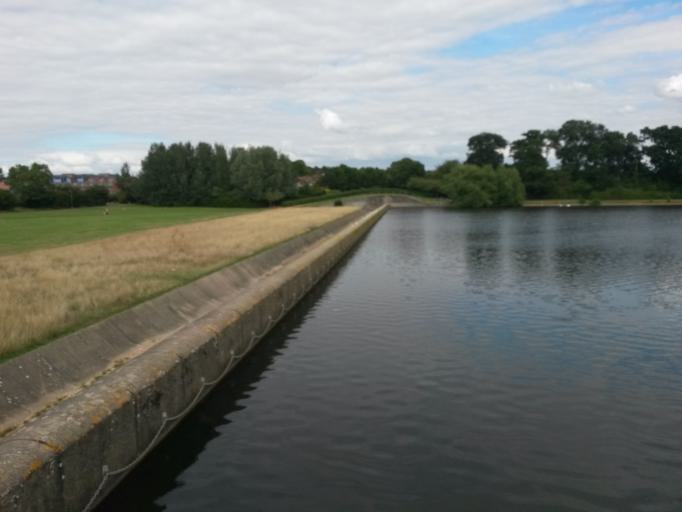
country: GB
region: England
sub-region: Milton Keynes
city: Simpson
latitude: 52.0150
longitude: -0.7075
